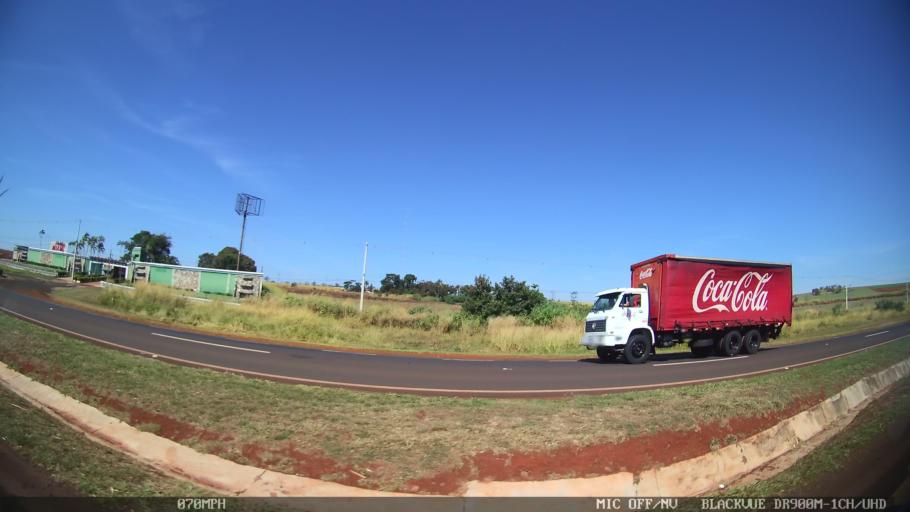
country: BR
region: Sao Paulo
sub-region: Ribeirao Preto
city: Ribeirao Preto
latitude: -21.1400
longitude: -47.8673
